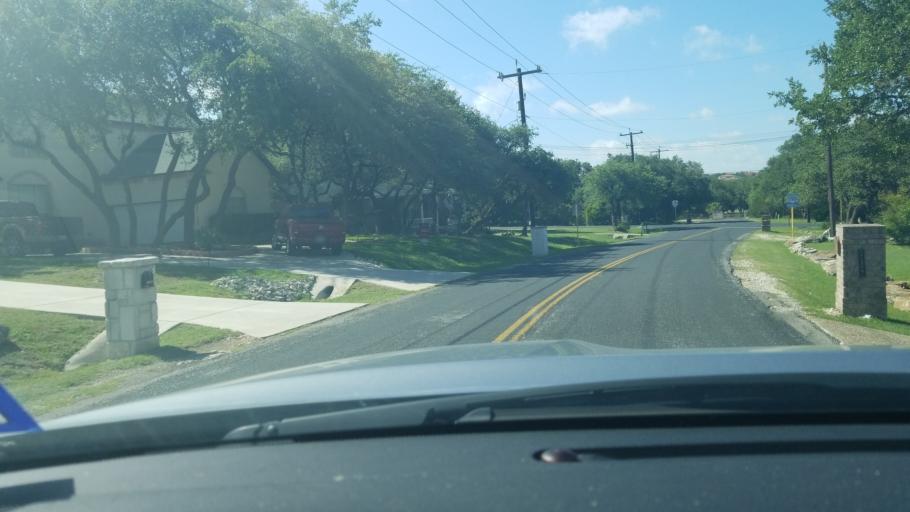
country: US
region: Texas
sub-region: Bexar County
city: Timberwood Park
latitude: 29.6858
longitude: -98.4857
